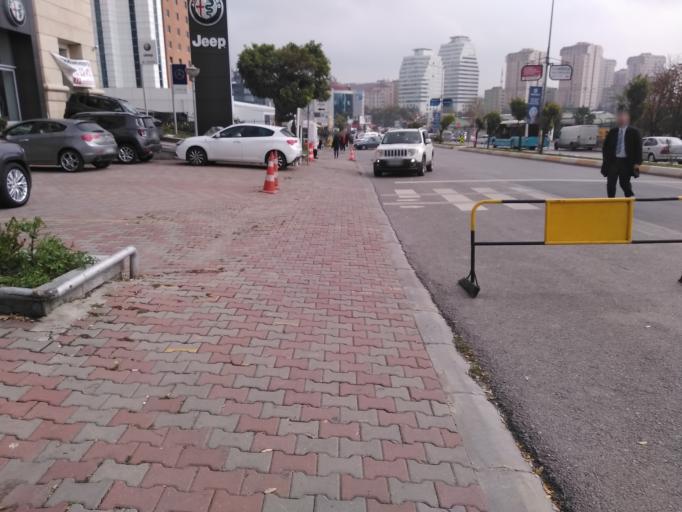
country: TR
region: Istanbul
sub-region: Atasehir
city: Atasehir
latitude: 40.9806
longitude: 29.1014
